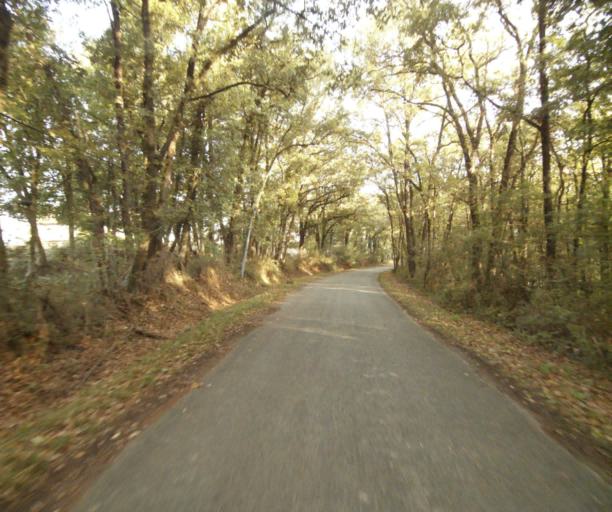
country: FR
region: Midi-Pyrenees
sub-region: Departement du Tarn-et-Garonne
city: Nohic
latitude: 43.9143
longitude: 1.4798
